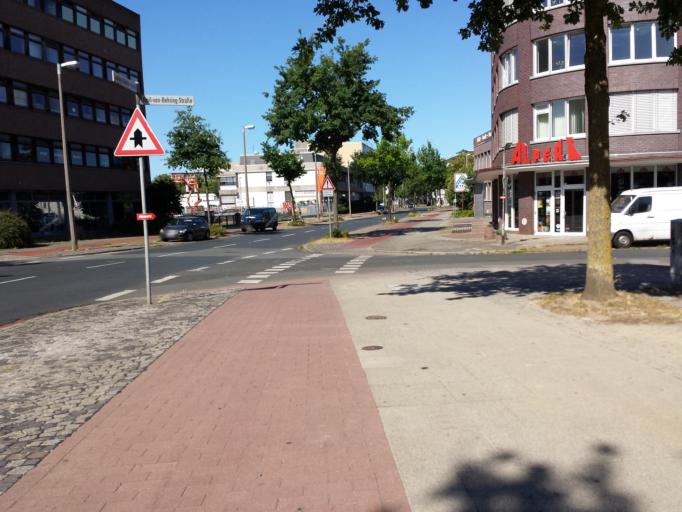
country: DE
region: Bremen
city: Bremen
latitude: 53.0683
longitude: 8.8635
